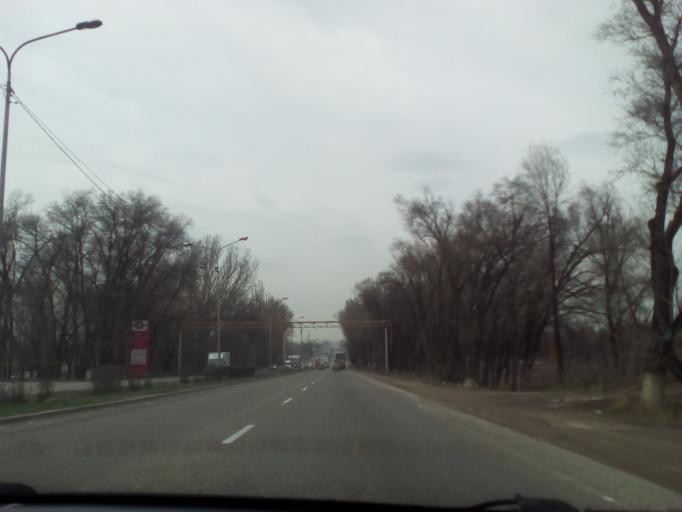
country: KZ
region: Almaty Oblysy
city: Burunday
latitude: 43.2168
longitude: 76.6595
